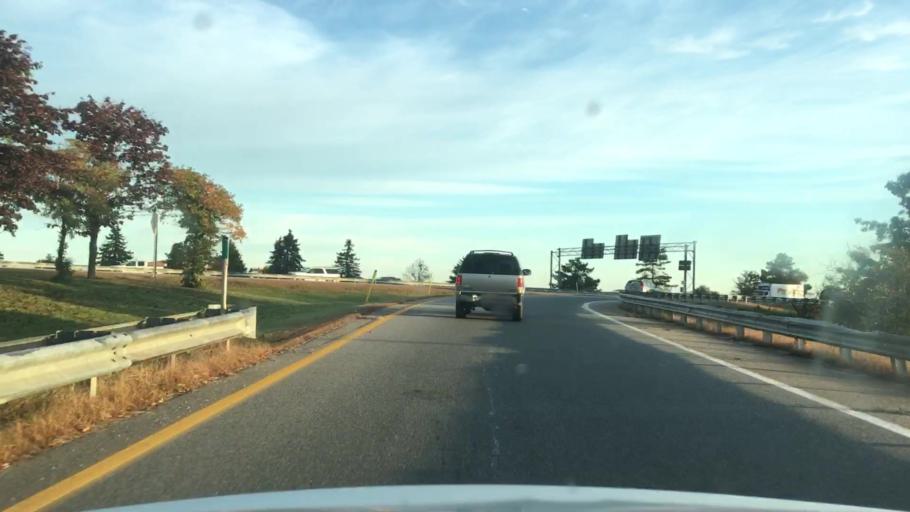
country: US
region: Maine
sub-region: Cumberland County
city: Portland
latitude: 43.6618
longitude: -70.2677
